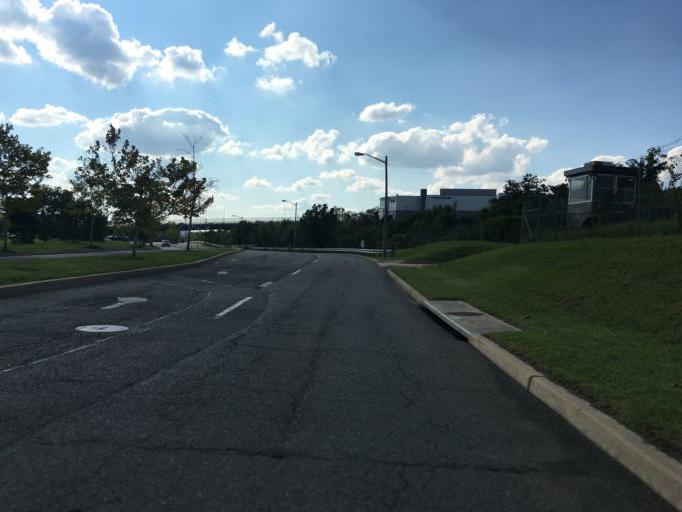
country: US
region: Virginia
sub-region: Fairfax County
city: Huntington
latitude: 38.8037
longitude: -77.0704
